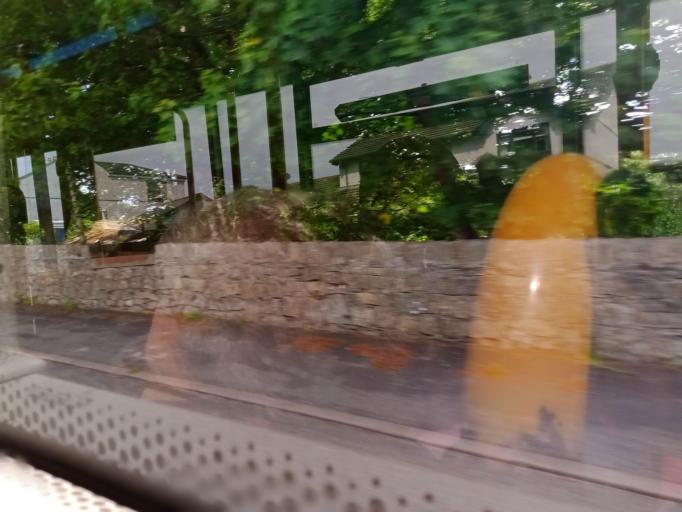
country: GB
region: Wales
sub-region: Gwynedd
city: Bangor
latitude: 53.2388
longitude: -4.1510
